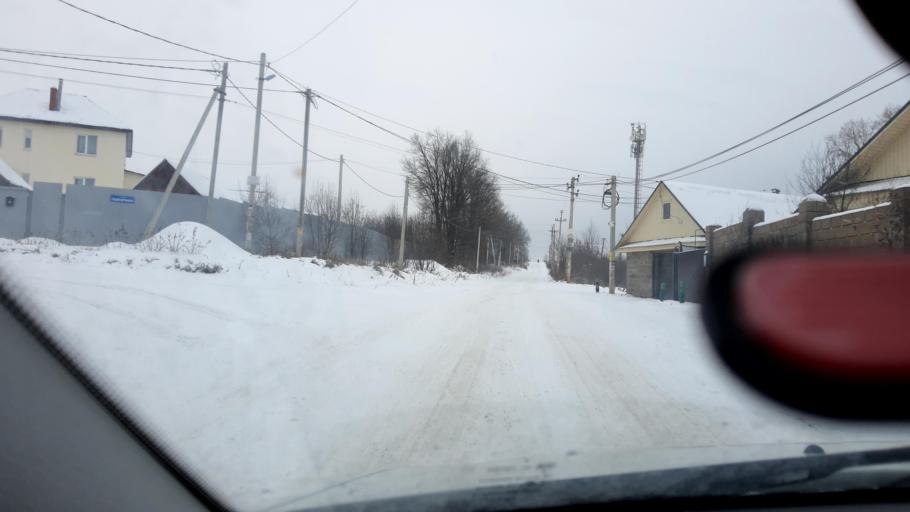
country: RU
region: Bashkortostan
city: Kabakovo
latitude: 54.6331
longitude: 56.0831
